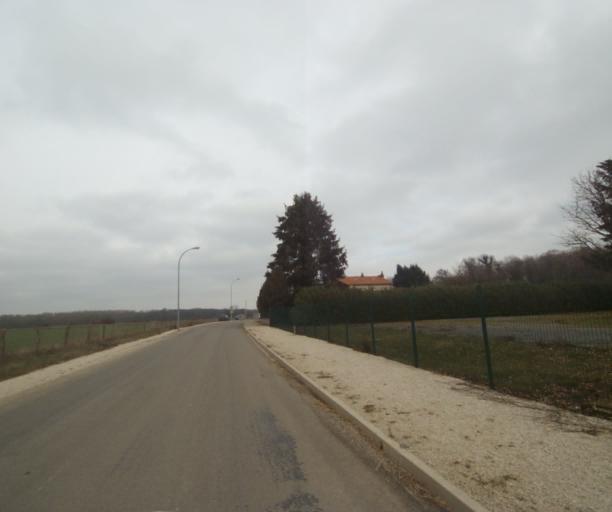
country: FR
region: Champagne-Ardenne
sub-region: Departement de la Haute-Marne
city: Villiers-en-Lieu
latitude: 48.6803
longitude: 4.8723
